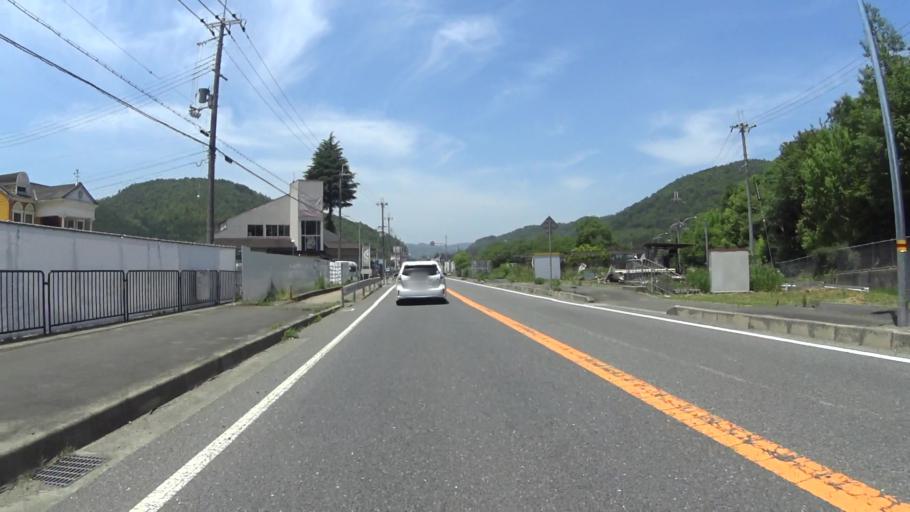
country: JP
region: Kyoto
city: Kameoka
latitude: 35.0900
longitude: 135.5014
